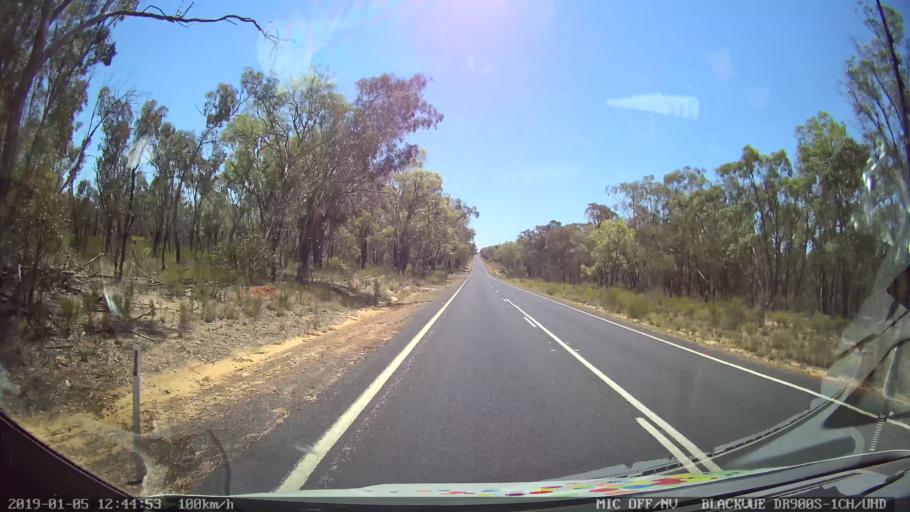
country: AU
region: New South Wales
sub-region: Warrumbungle Shire
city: Coonabarabran
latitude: -31.1333
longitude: 149.5429
